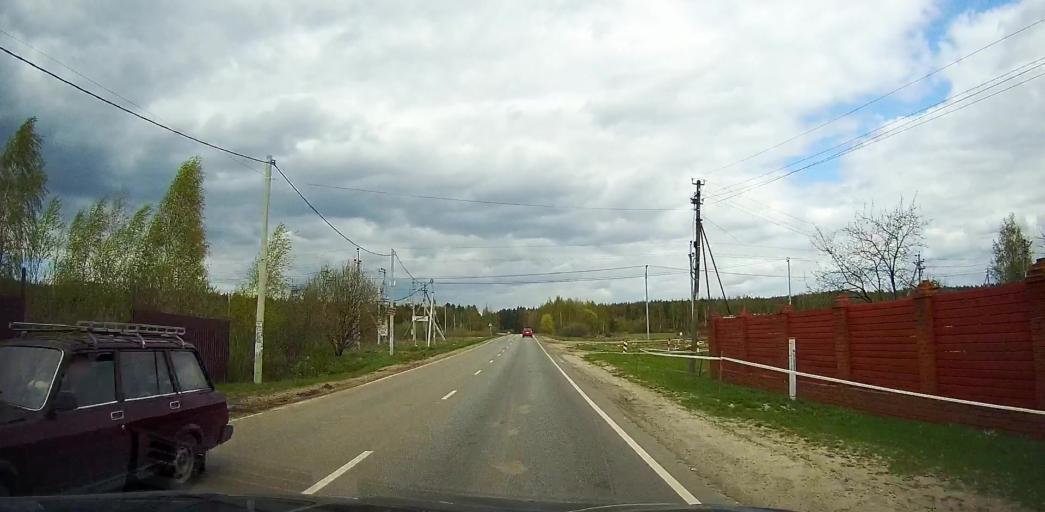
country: RU
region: Moskovskaya
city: Ashitkovo
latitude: 55.4657
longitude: 38.6072
